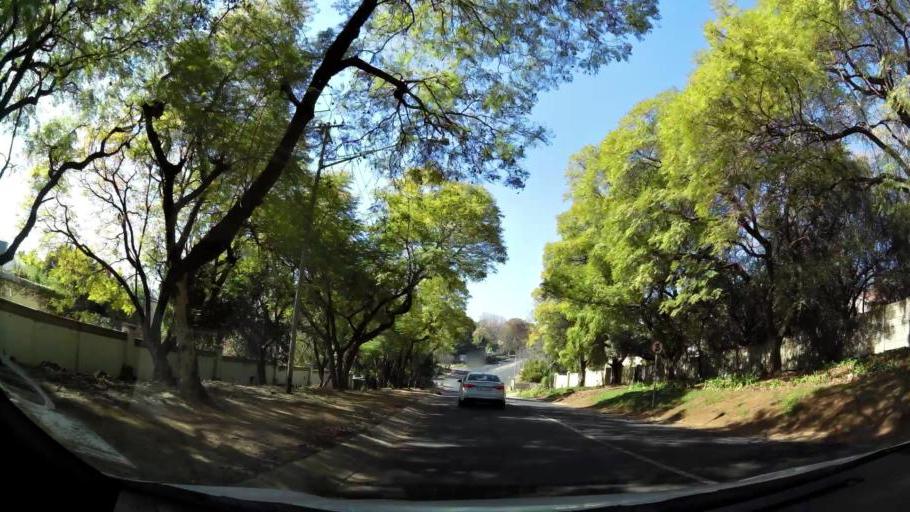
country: ZA
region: Gauteng
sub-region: City of Tshwane Metropolitan Municipality
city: Pretoria
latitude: -25.7819
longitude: 28.2301
